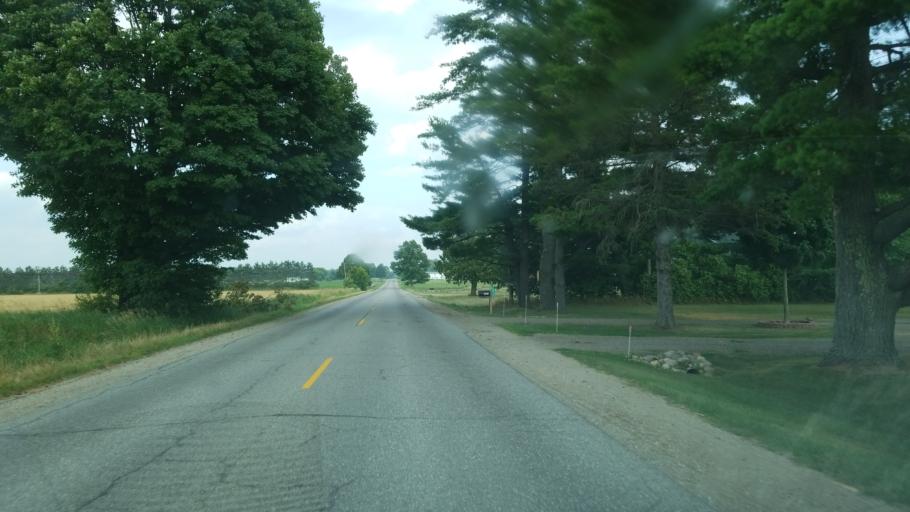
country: US
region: Michigan
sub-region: Mecosta County
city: Canadian Lakes
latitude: 43.5424
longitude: -85.3510
